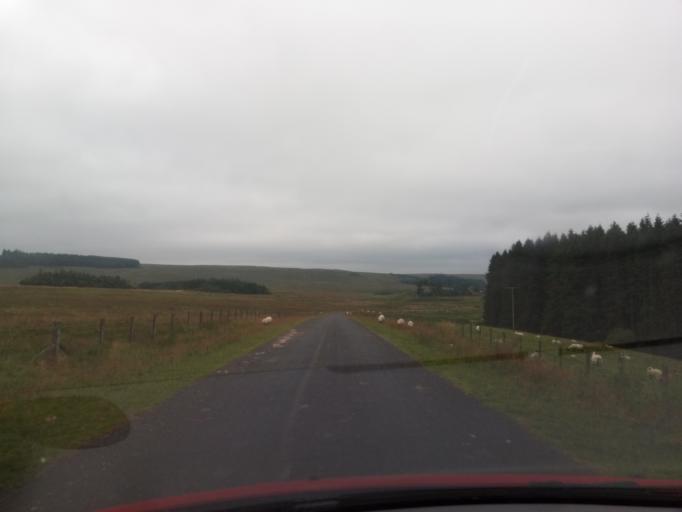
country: GB
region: England
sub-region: Northumberland
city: Rochester
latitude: 55.2894
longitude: -2.2159
